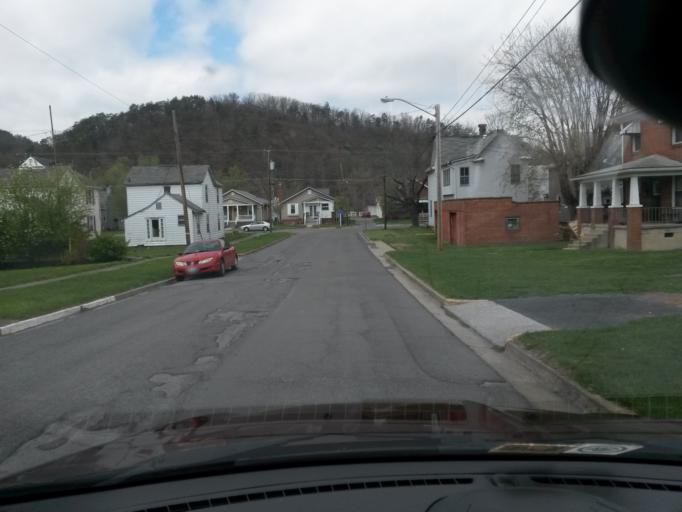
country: US
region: Virginia
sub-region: City of Covington
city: Covington
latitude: 37.7894
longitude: -79.9985
